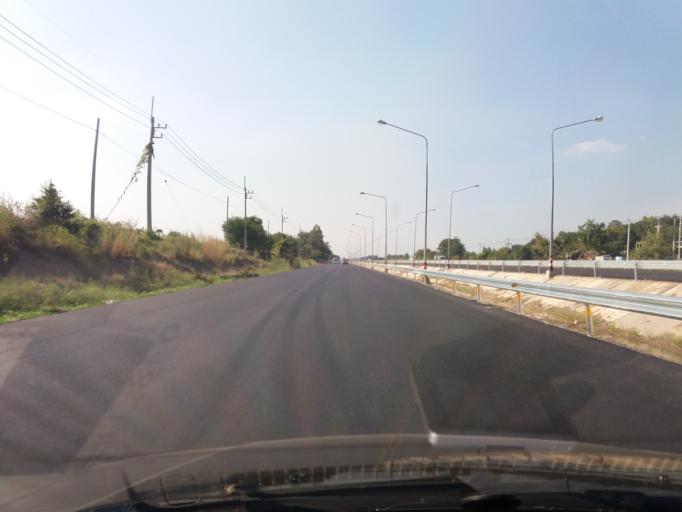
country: TH
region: Nakhon Sawan
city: Krok Phra
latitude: 15.6188
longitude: 100.1177
